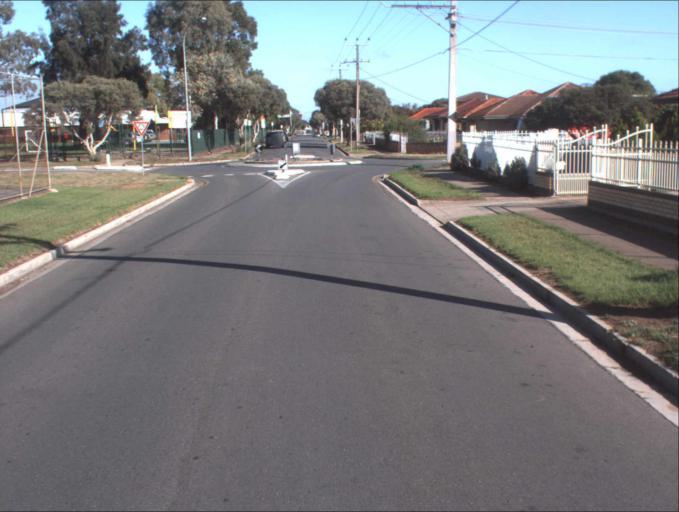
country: AU
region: South Australia
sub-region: Charles Sturt
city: Woodville North
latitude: -34.8539
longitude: 138.5534
